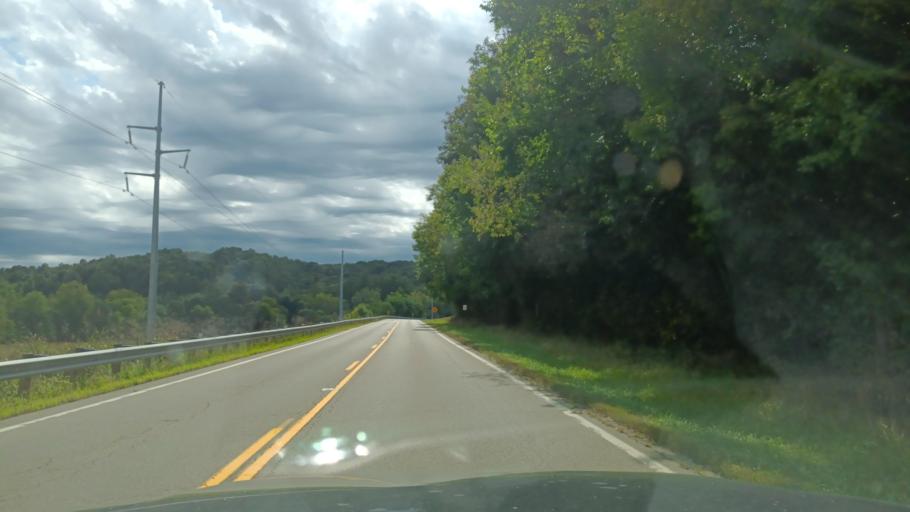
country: US
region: Ohio
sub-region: Vinton County
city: McArthur
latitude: 39.2385
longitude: -82.3717
